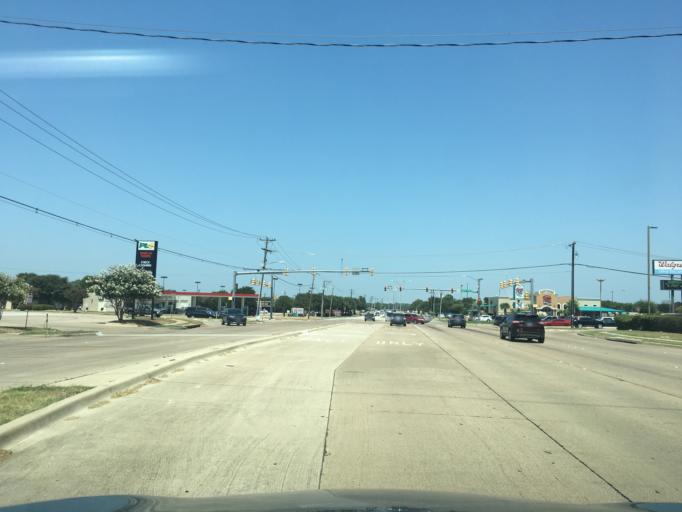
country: US
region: Texas
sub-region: Tarrant County
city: Edgecliff Village
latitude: 32.6340
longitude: -97.3698
